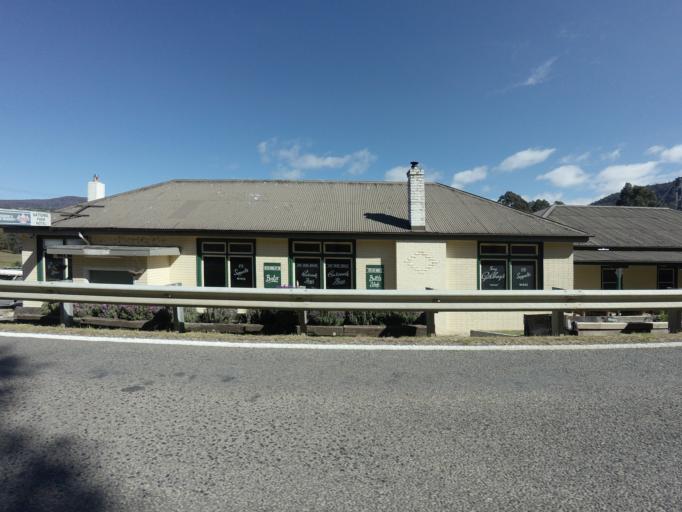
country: AU
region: Tasmania
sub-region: Derwent Valley
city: New Norfolk
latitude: -42.6858
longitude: 146.7190
